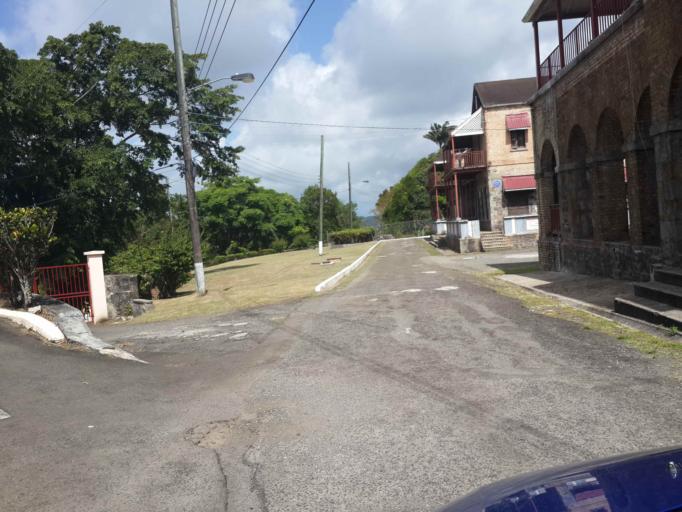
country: LC
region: Castries Quarter
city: Castries
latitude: 13.9975
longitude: -60.9943
